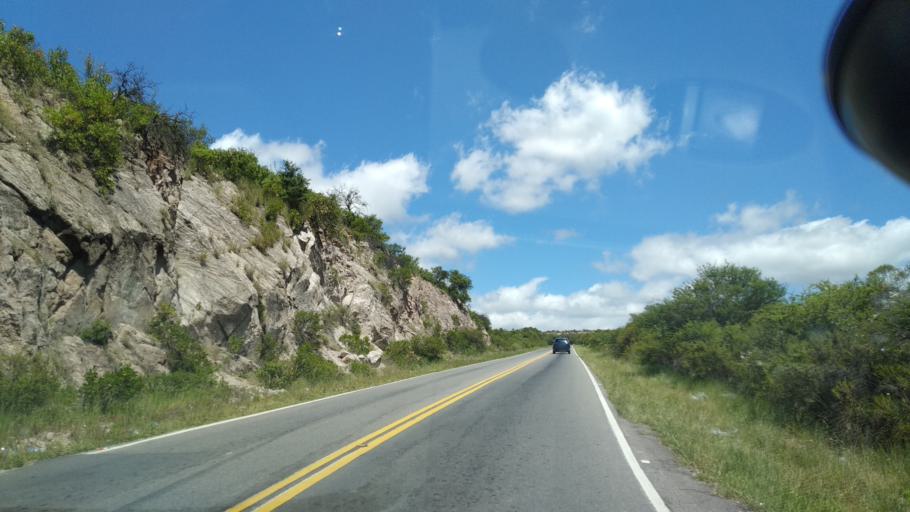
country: AR
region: Cordoba
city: Villa Cura Brochero
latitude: -31.6989
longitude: -65.0534
